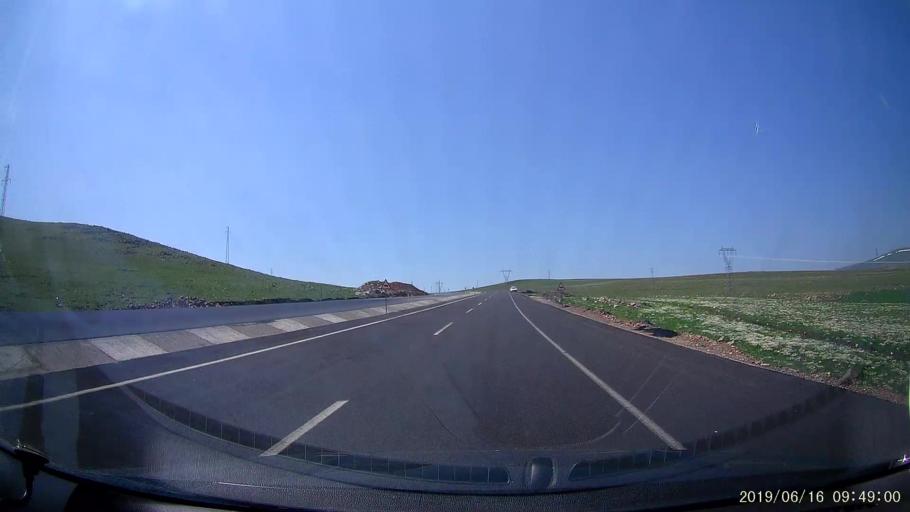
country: TR
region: Kars
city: Digor
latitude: 40.4266
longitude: 43.3562
